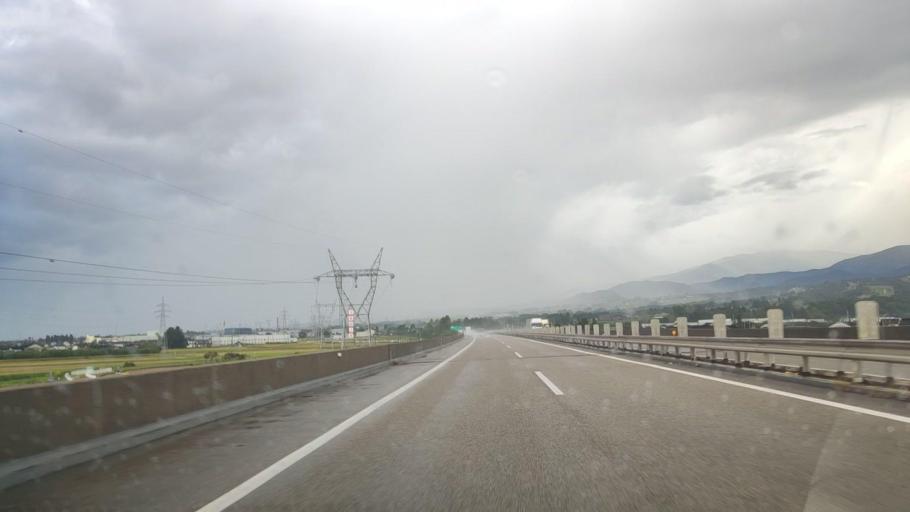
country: JP
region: Toyama
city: Kamiichi
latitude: 36.7267
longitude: 137.3638
